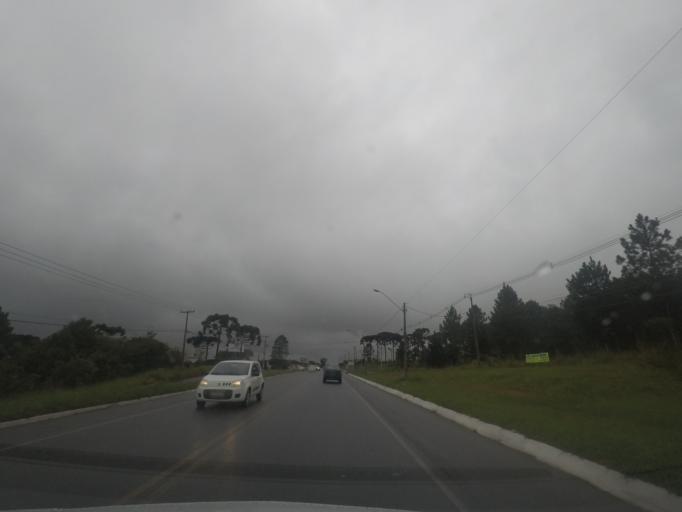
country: BR
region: Parana
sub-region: Colombo
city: Colombo
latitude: -25.3464
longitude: -49.1611
